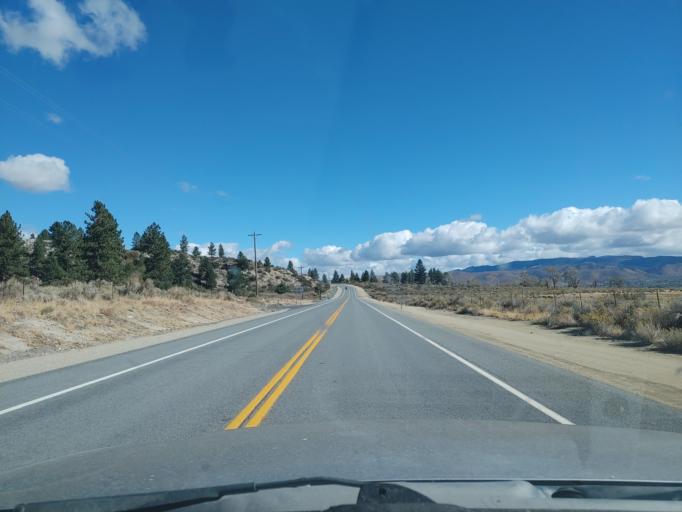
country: US
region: Nevada
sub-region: Washoe County
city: Incline Village
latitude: 39.2882
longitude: -119.8360
